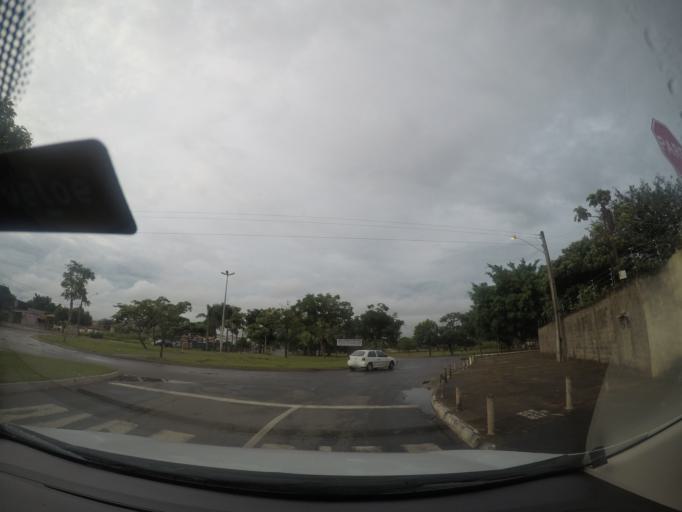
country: BR
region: Goias
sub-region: Goiania
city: Goiania
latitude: -16.6903
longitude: -49.3511
